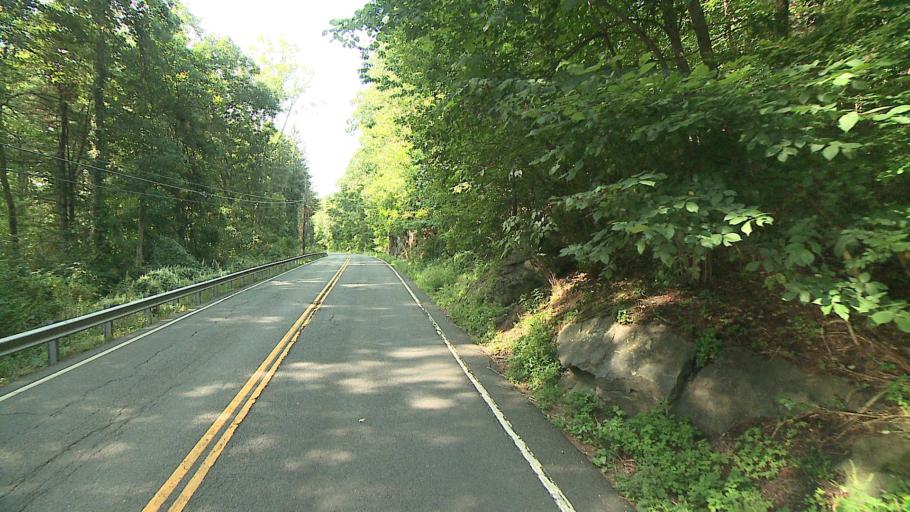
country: US
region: Connecticut
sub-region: Litchfield County
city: Canaan
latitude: 41.9225
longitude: -73.3641
